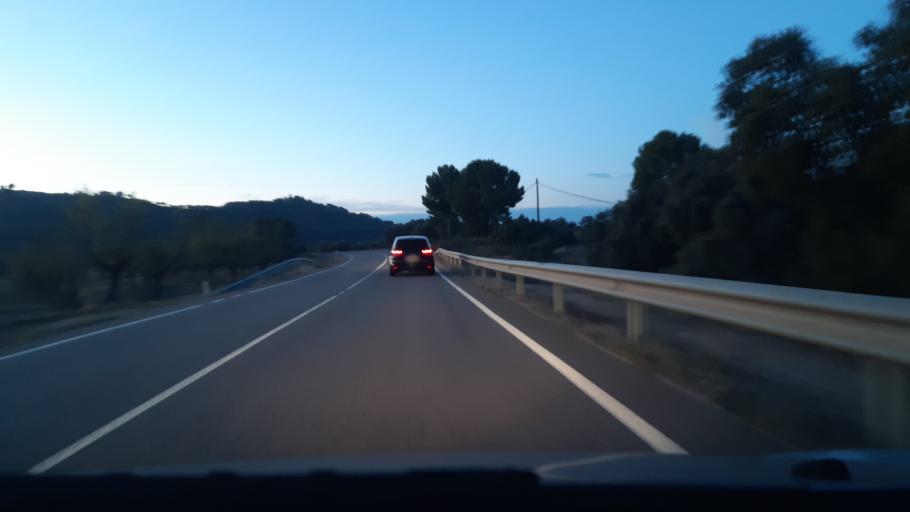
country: ES
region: Aragon
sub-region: Provincia de Teruel
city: Calaceite
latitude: 40.9997
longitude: 0.1951
